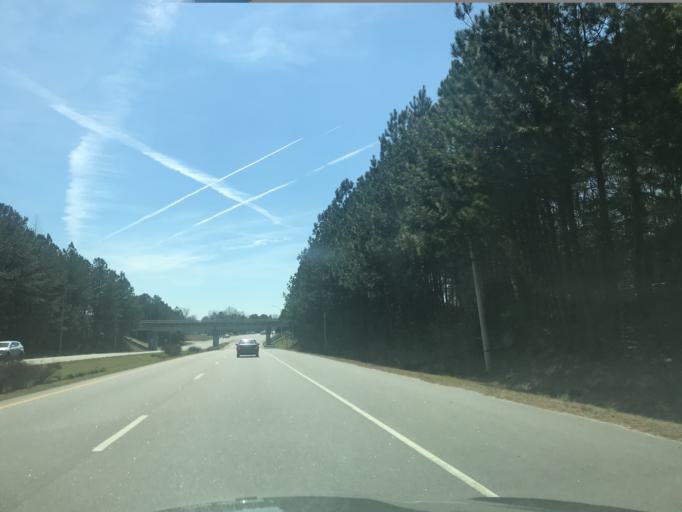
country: US
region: North Carolina
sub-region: Wake County
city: Fuquay-Varina
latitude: 35.5995
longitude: -78.7554
